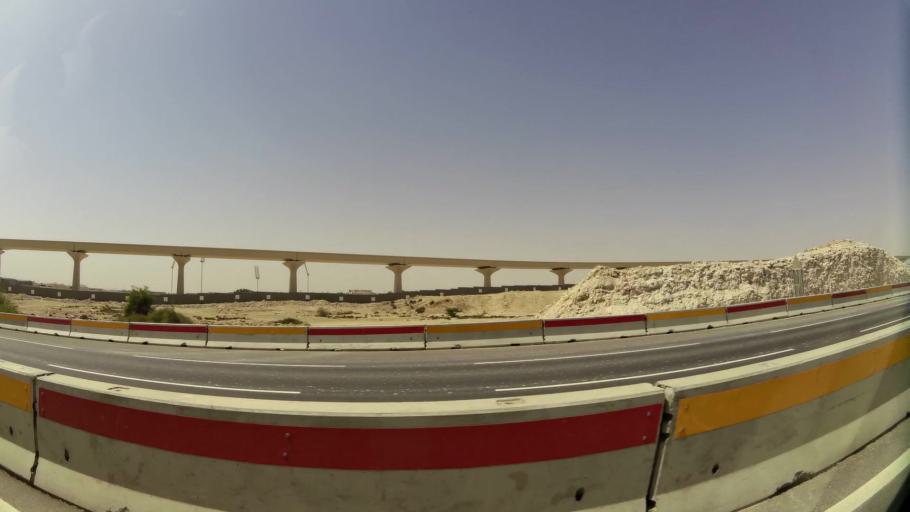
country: QA
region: Baladiyat Umm Salal
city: Umm Salal Muhammad
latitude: 25.3801
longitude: 51.4978
